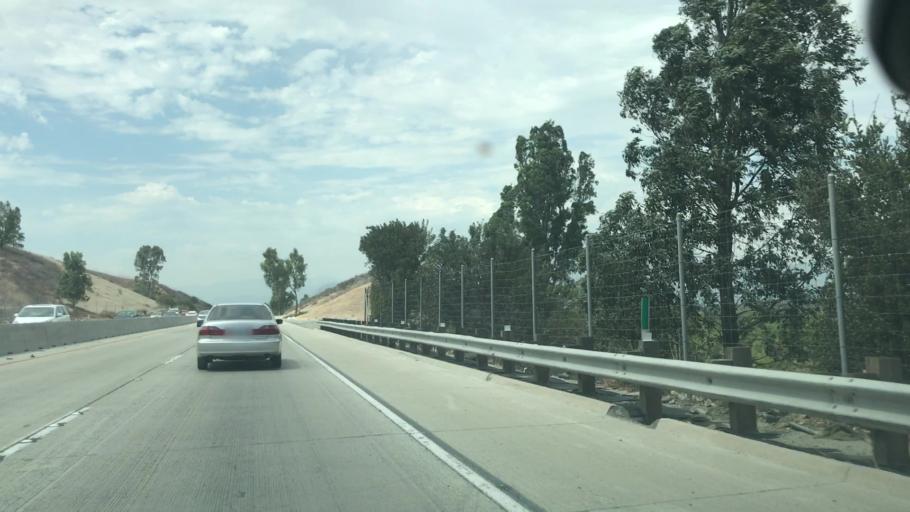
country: US
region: California
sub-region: Riverside County
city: Corona
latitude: 33.9068
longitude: -117.6486
